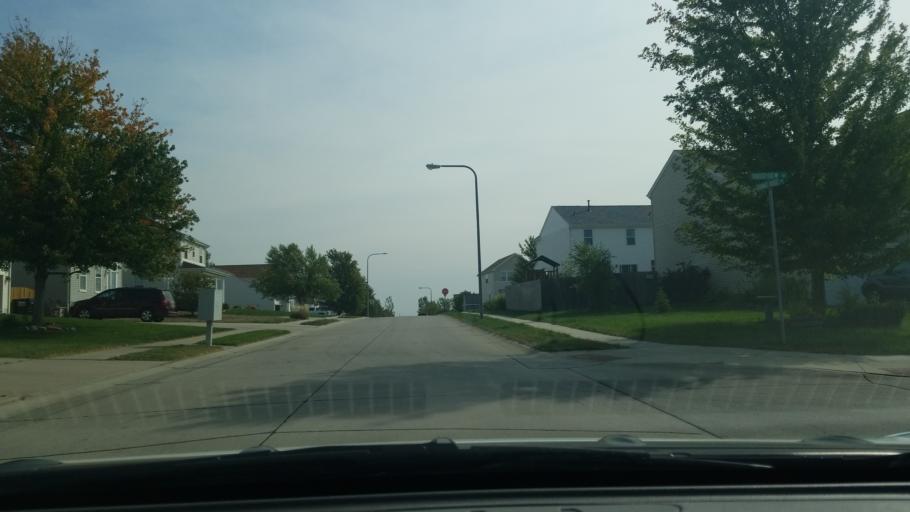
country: US
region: Nebraska
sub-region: Sarpy County
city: Papillion
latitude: 41.1286
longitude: -96.0566
